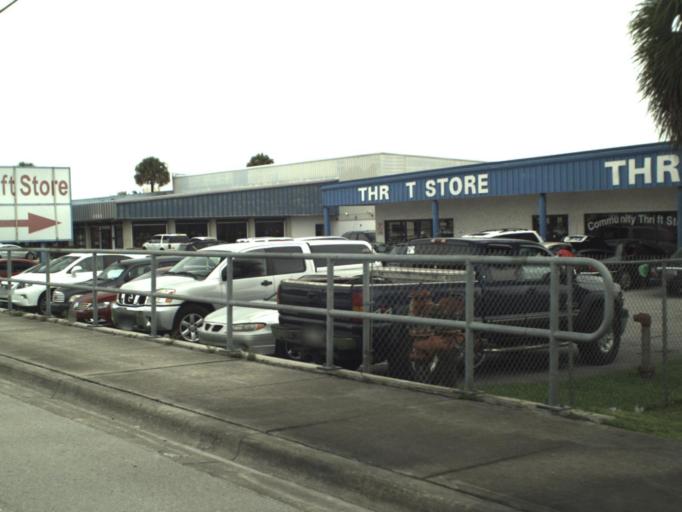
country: US
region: Florida
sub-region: Palm Beach County
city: Mangonia Park
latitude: 26.7742
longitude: -80.1075
